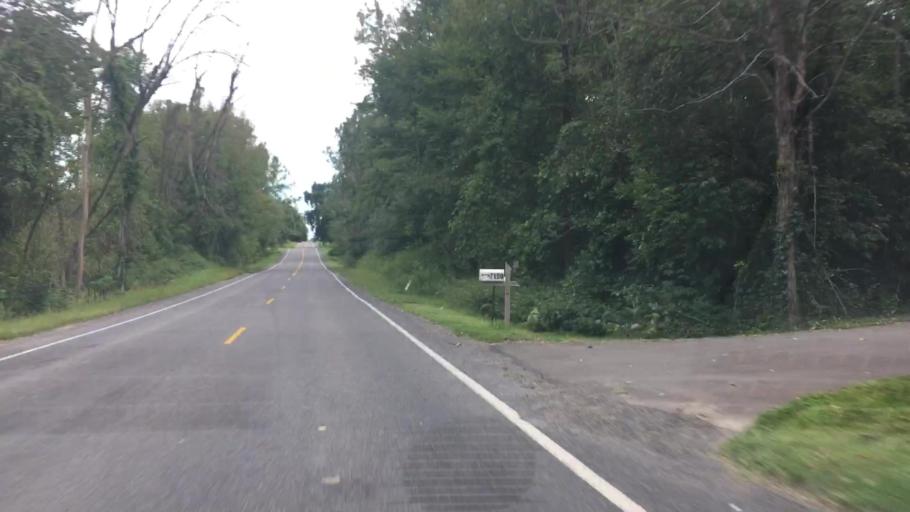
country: US
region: Michigan
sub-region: Kent County
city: Byron Center
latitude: 42.8354
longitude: -85.7825
